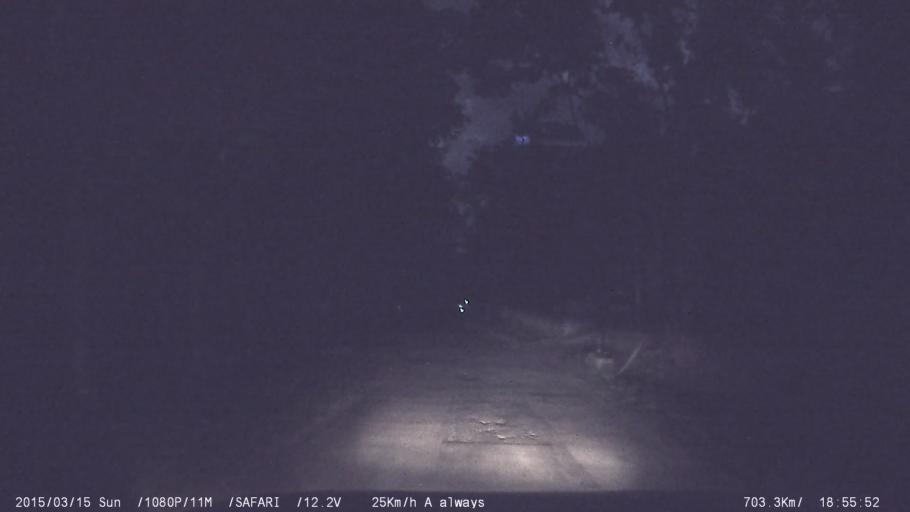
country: IN
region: Kerala
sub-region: Kottayam
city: Palackattumala
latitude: 9.8600
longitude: 76.6752
